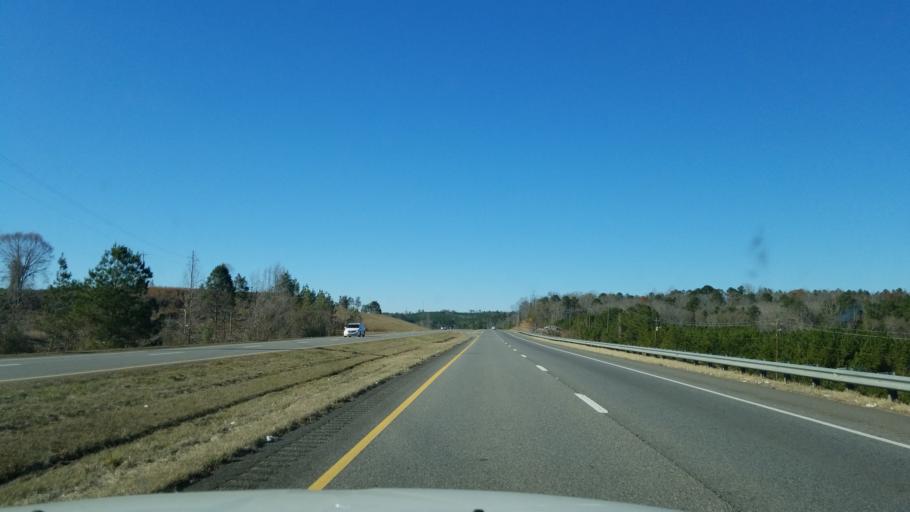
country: US
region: Alabama
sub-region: Tuscaloosa County
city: Northport
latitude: 33.2615
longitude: -87.7048
